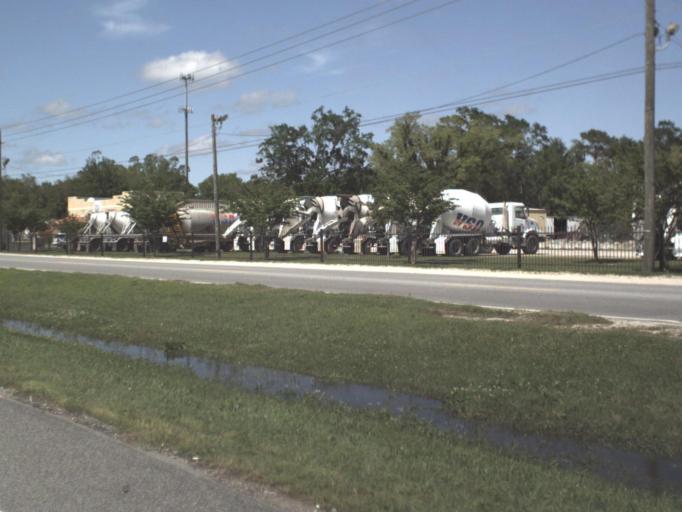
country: US
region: Florida
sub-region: Escambia County
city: Gonzalez
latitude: 30.5579
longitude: -87.2852
